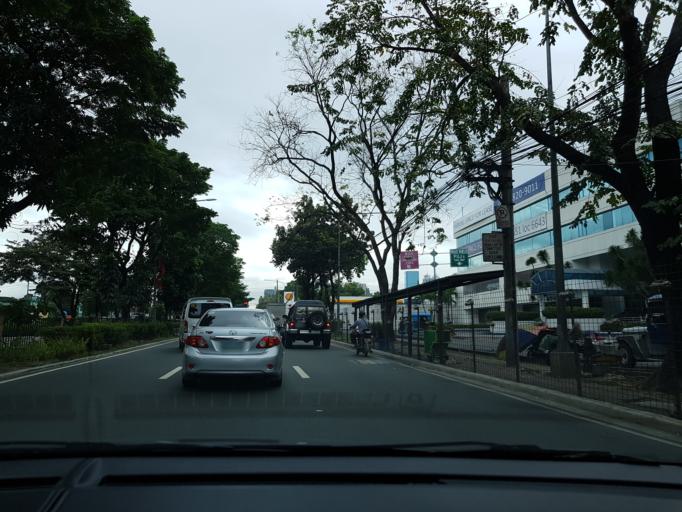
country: PH
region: Metro Manila
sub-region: San Juan
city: San Juan
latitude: 14.6004
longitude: 121.0487
